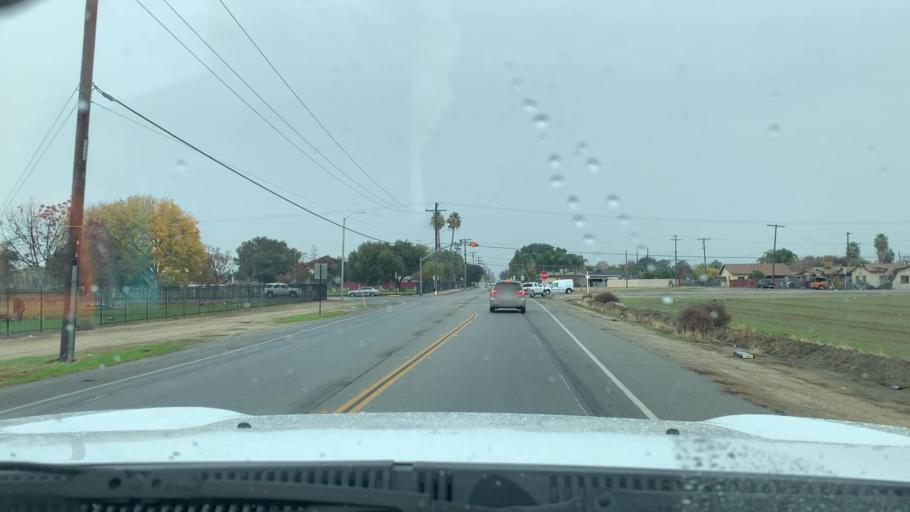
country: US
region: California
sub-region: Kern County
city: Delano
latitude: 35.7614
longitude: -119.2596
